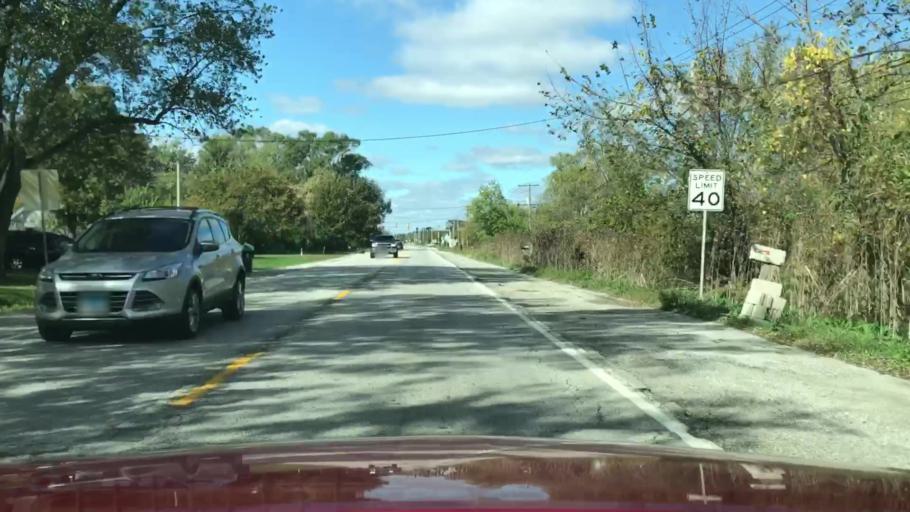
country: US
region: Illinois
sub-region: Cook County
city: Ford Heights
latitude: 41.5304
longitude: -87.5749
